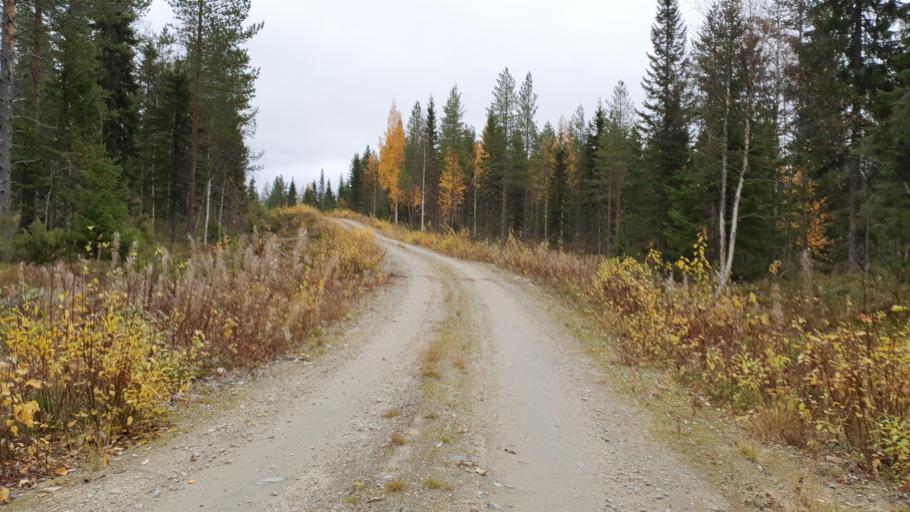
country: FI
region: Kainuu
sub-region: Kehys-Kainuu
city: Kuhmo
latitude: 64.4449
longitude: 29.6282
